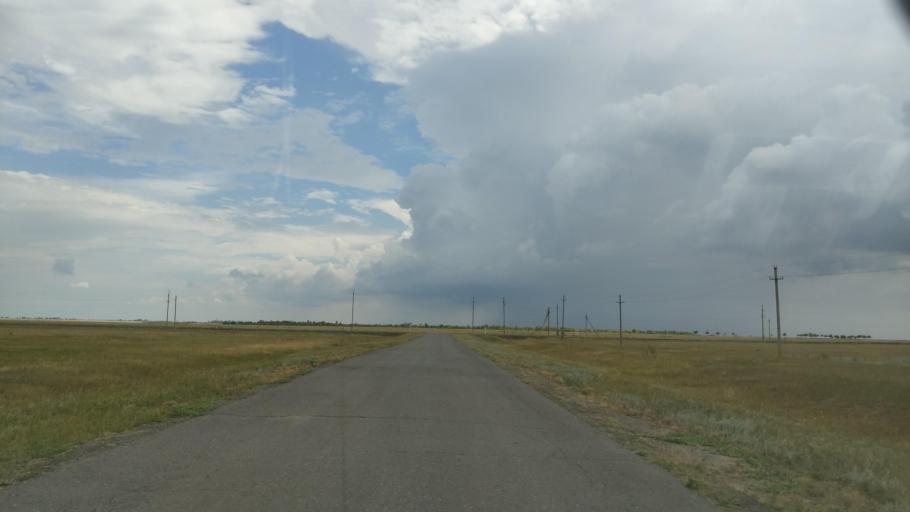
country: KZ
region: Pavlodar
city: Pavlodar
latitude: 52.6332
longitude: 77.3452
